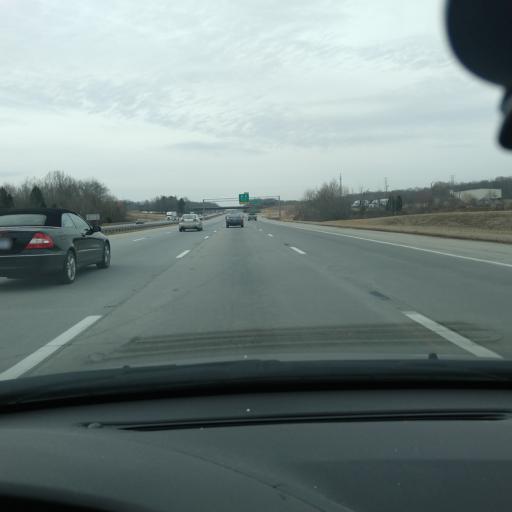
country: US
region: North Carolina
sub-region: Rowan County
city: China Grove
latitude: 35.6037
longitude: -80.5268
